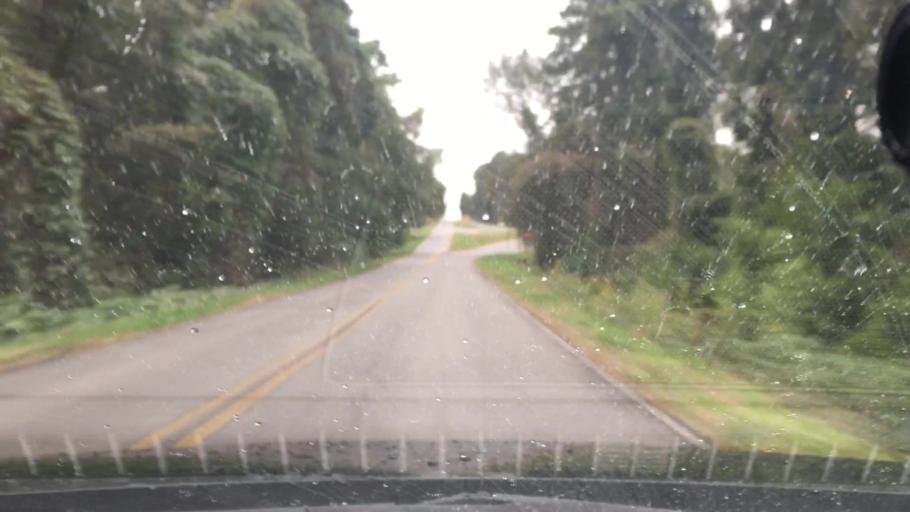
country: US
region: Georgia
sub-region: Spalding County
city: Experiment
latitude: 33.2389
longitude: -84.3189
